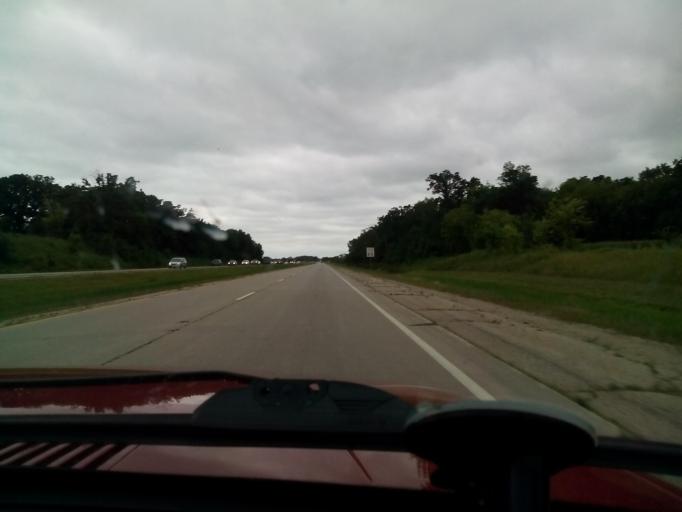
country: US
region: Wisconsin
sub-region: Dane County
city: Marshall
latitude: 43.2613
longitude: -89.1167
